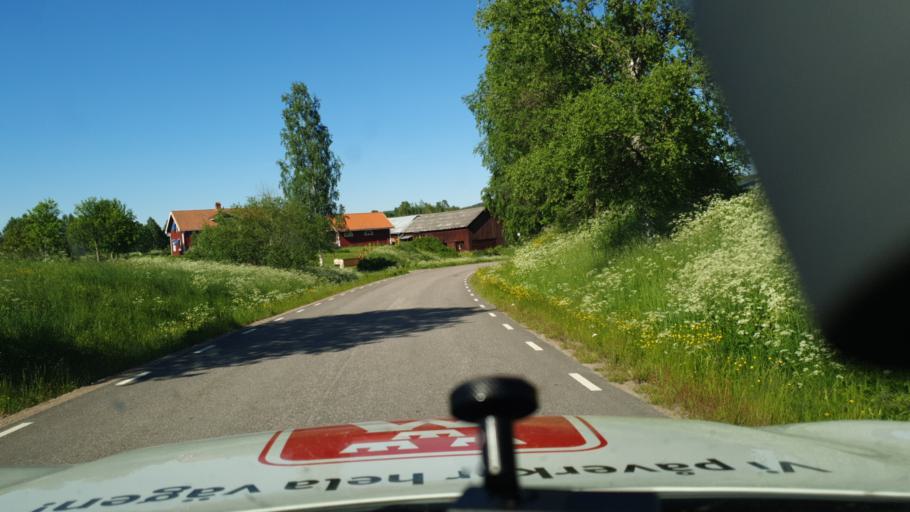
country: SE
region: Vaermland
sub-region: Torsby Kommun
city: Torsby
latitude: 60.1650
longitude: 13.0256
